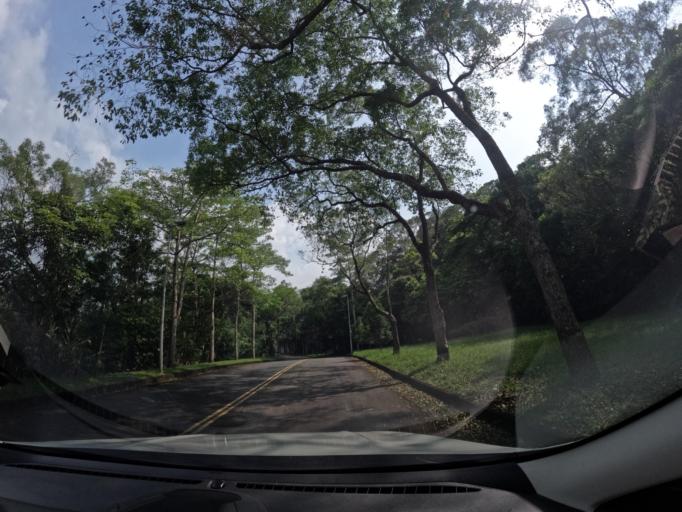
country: TW
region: Taiwan
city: Daxi
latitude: 24.8927
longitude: 121.3229
